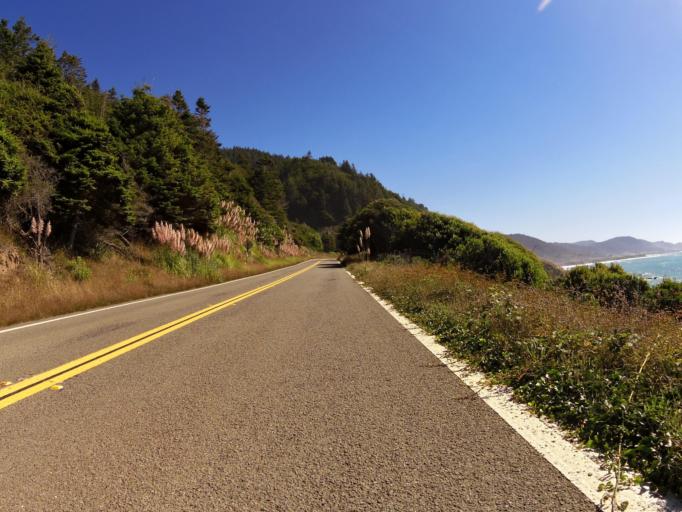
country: US
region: California
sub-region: Mendocino County
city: Fort Bragg
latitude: 39.6997
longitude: -123.8022
